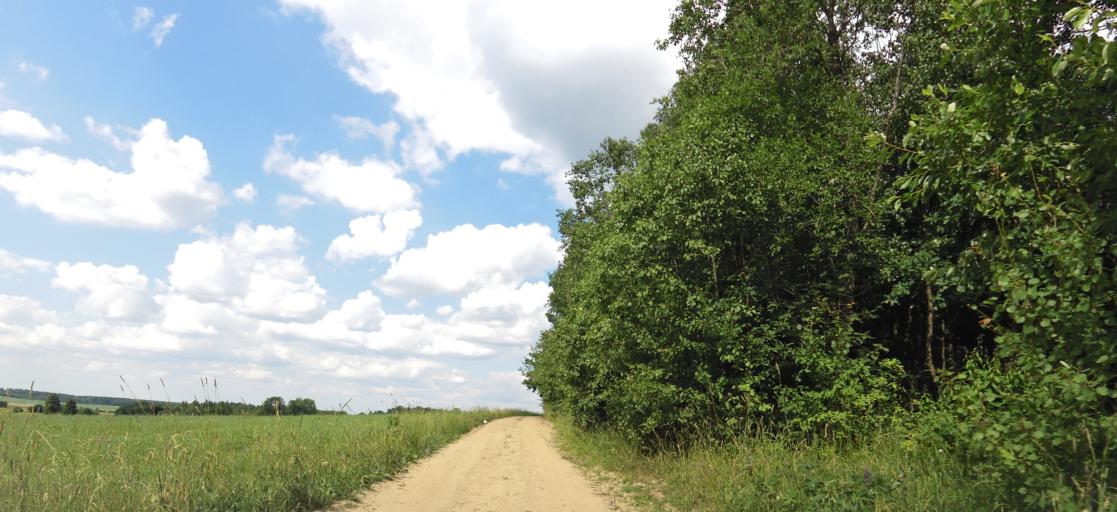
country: LT
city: Skaidiskes
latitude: 54.5273
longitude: 25.6221
